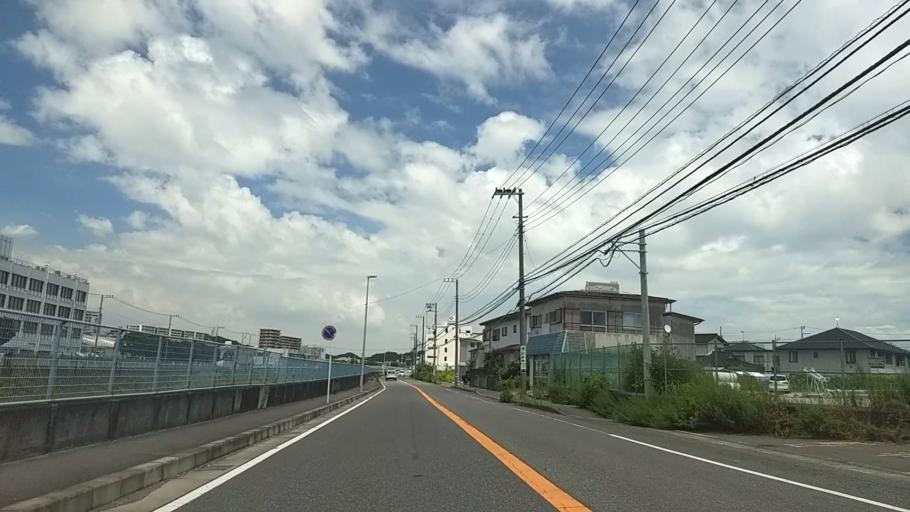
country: JP
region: Kanagawa
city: Fujisawa
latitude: 35.3368
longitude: 139.5129
